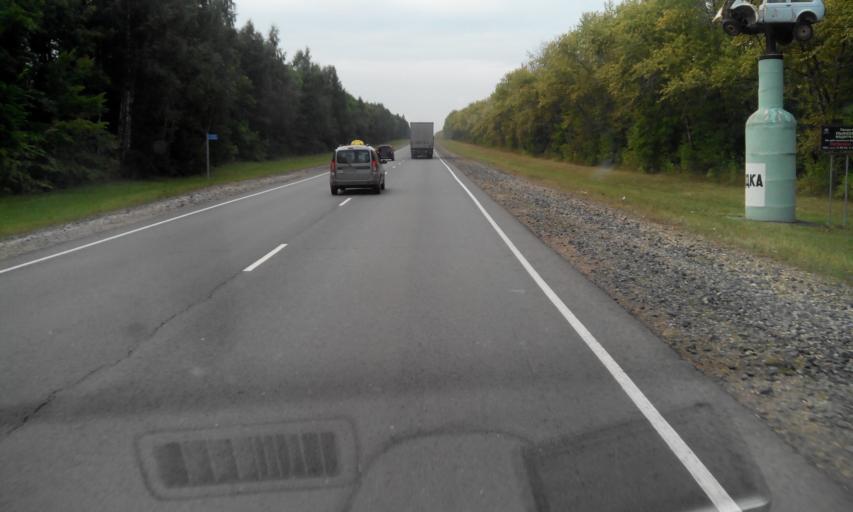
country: RU
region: Penza
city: Poselki
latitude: 53.1081
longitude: 46.4688
